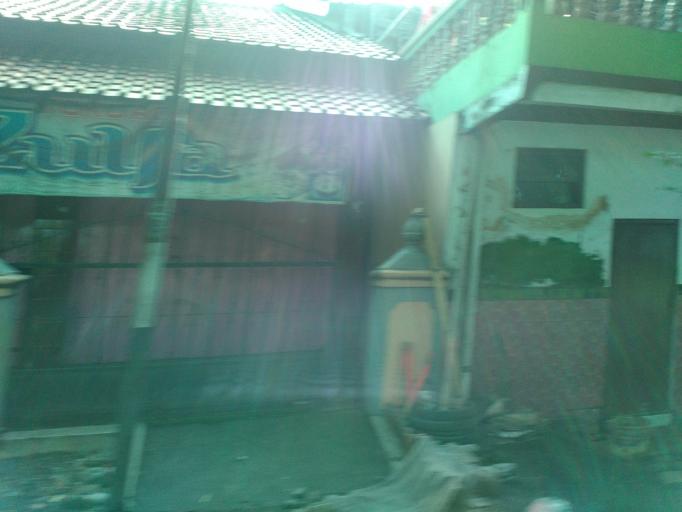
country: ID
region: Central Java
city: Gatak
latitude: -7.6036
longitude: 110.7028
